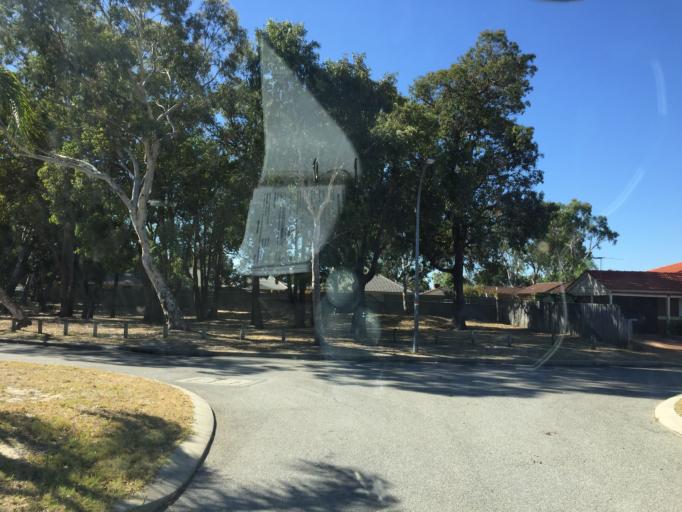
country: AU
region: Western Australia
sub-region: Swan
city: Stratton
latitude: -31.8653
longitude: 116.0426
